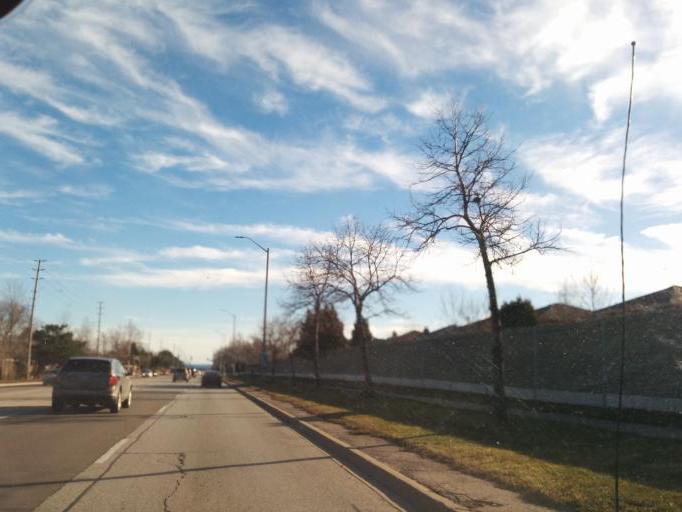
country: CA
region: Ontario
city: Oakville
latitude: 43.5068
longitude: -79.6599
